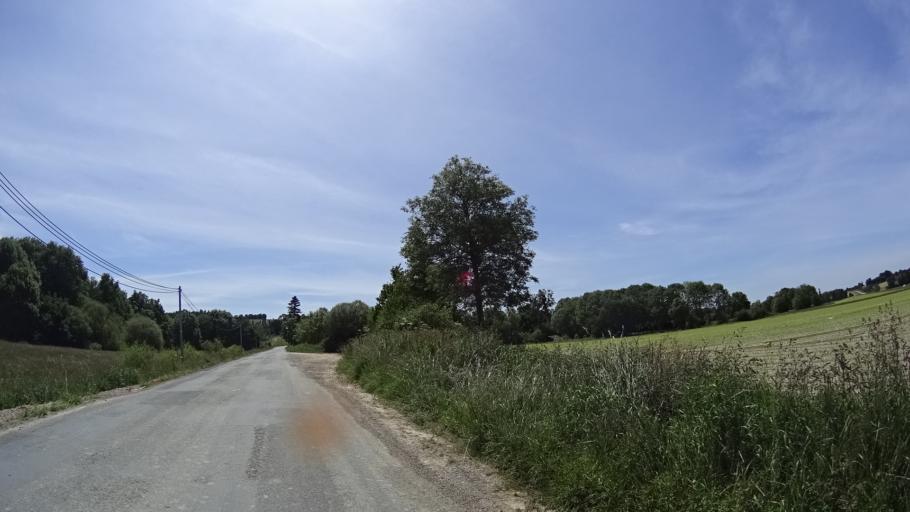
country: FR
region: Brittany
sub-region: Departement d'Ille-et-Vilaine
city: Montfort-sur-Meu
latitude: 48.1381
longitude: -1.9910
